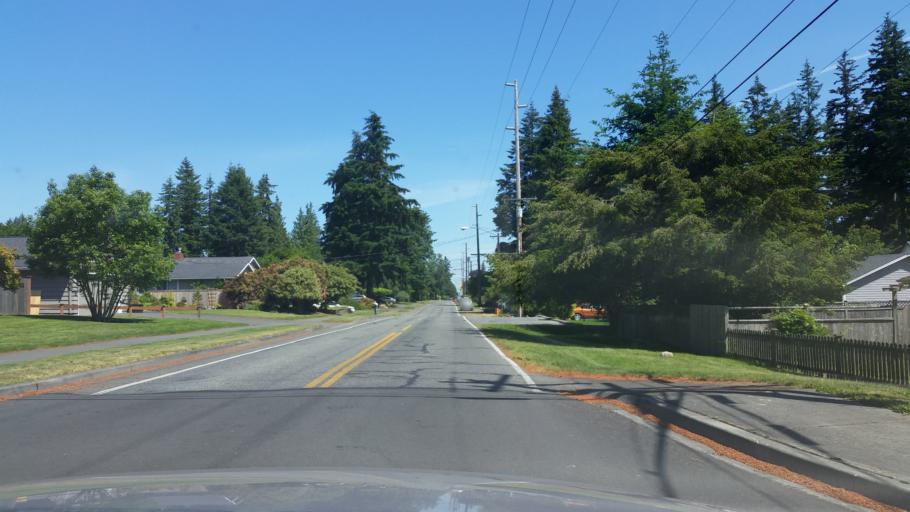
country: US
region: Washington
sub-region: Snohomish County
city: Esperance
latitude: 47.7959
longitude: -122.3616
